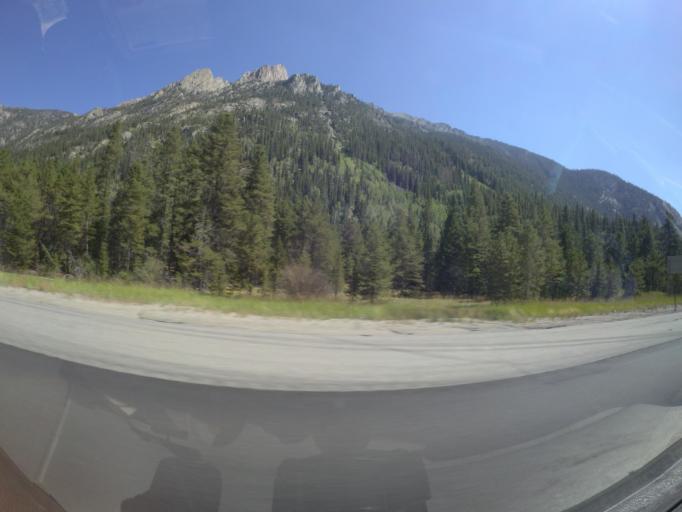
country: US
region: Colorado
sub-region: Summit County
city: Frisco
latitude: 39.5473
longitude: -106.1398
